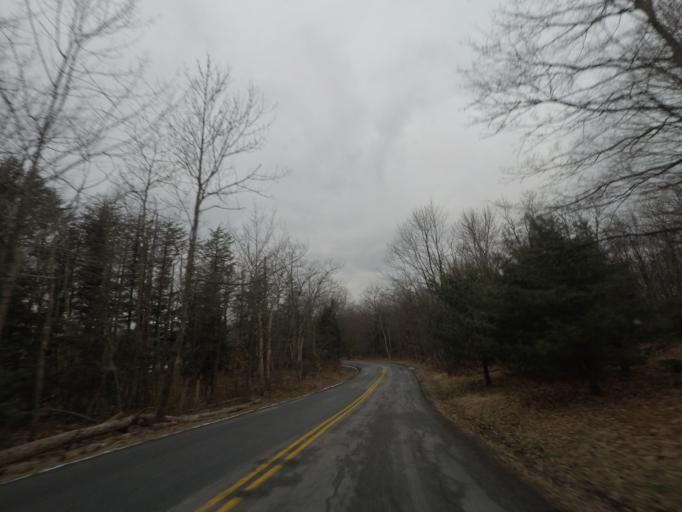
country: US
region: New York
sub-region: Rensselaer County
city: Poestenkill
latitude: 42.7327
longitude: -73.5063
